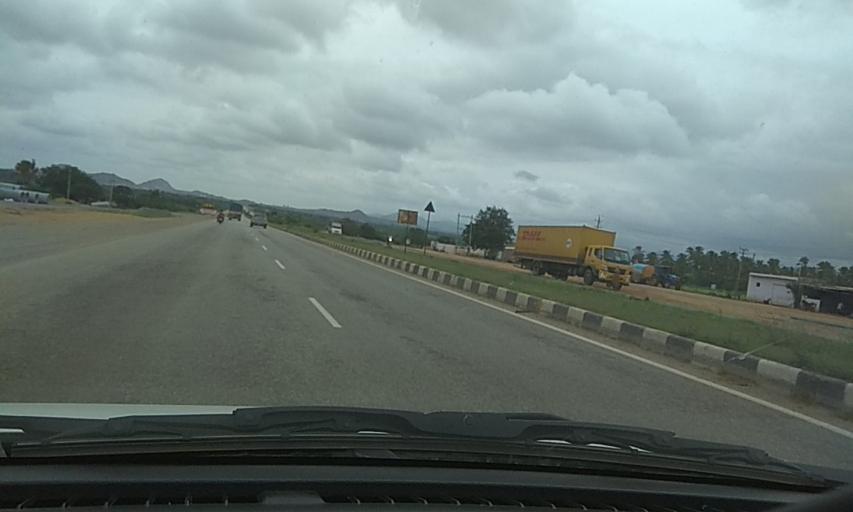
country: IN
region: Karnataka
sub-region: Chitradurga
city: Chitradurga
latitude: 14.2800
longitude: 76.3089
